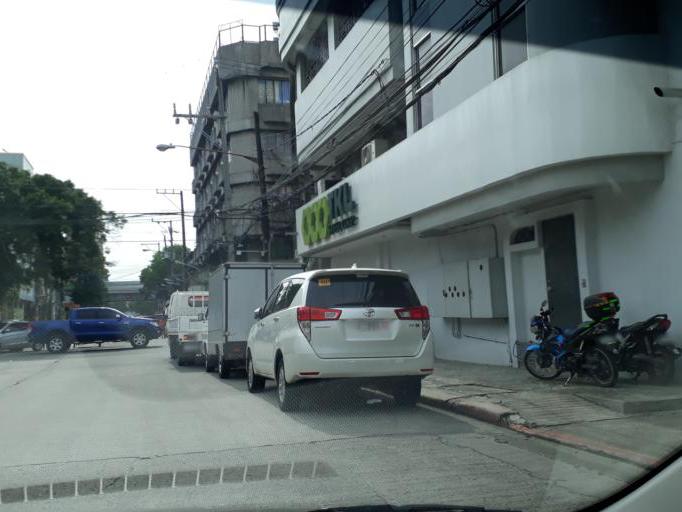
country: PH
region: Metro Manila
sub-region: City of Manila
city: Manila
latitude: 14.6206
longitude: 120.9843
